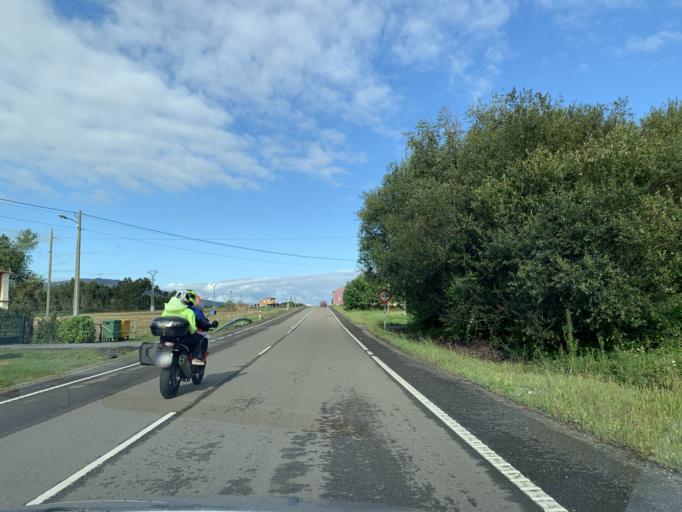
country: ES
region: Galicia
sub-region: Provincia de Lugo
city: Ribadeo
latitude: 43.5464
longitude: -7.0969
